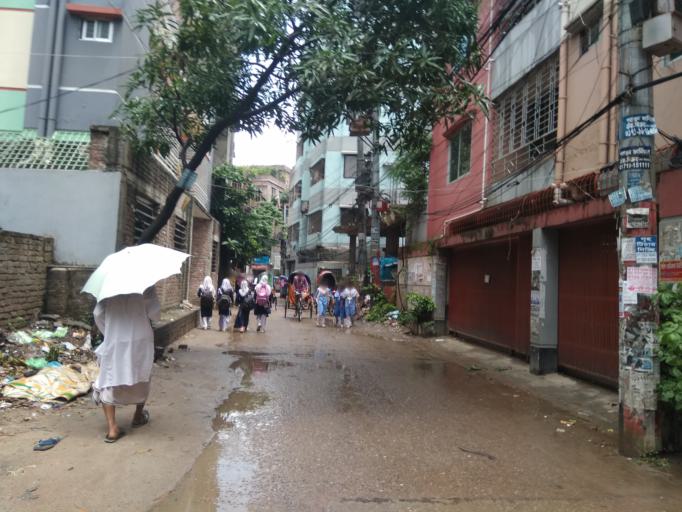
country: BD
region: Dhaka
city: Azimpur
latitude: 23.7973
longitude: 90.3769
